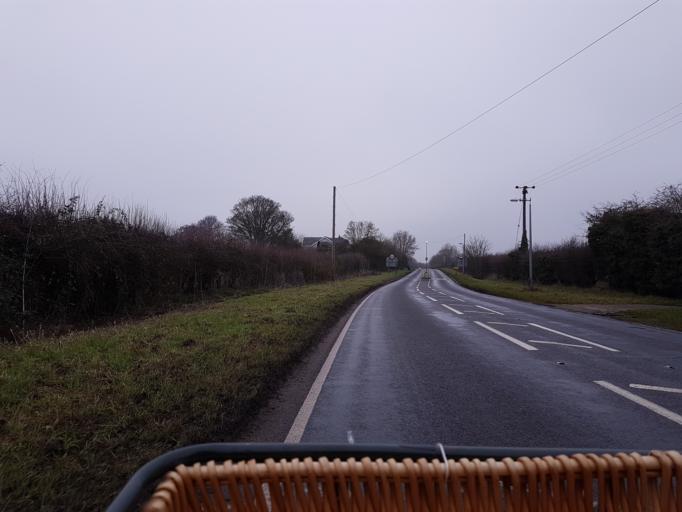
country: GB
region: England
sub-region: Cambridgeshire
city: Duxford
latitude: 52.0670
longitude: 0.1928
